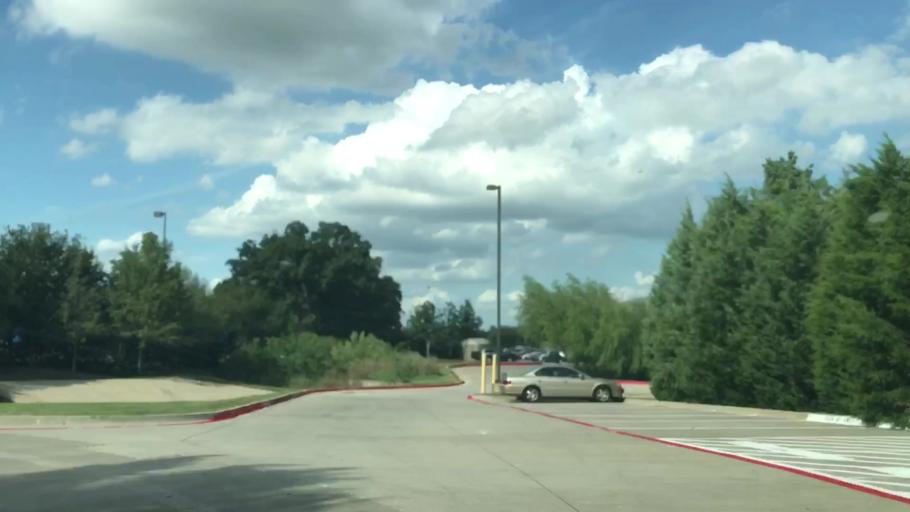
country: US
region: Texas
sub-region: Dallas County
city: Coppell
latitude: 32.9739
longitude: -97.0198
